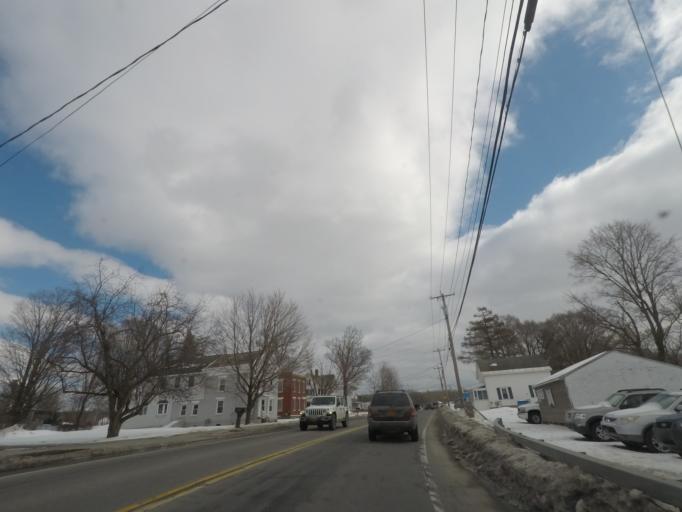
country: US
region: New York
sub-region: Washington County
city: Greenwich
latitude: 43.1038
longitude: -73.5221
